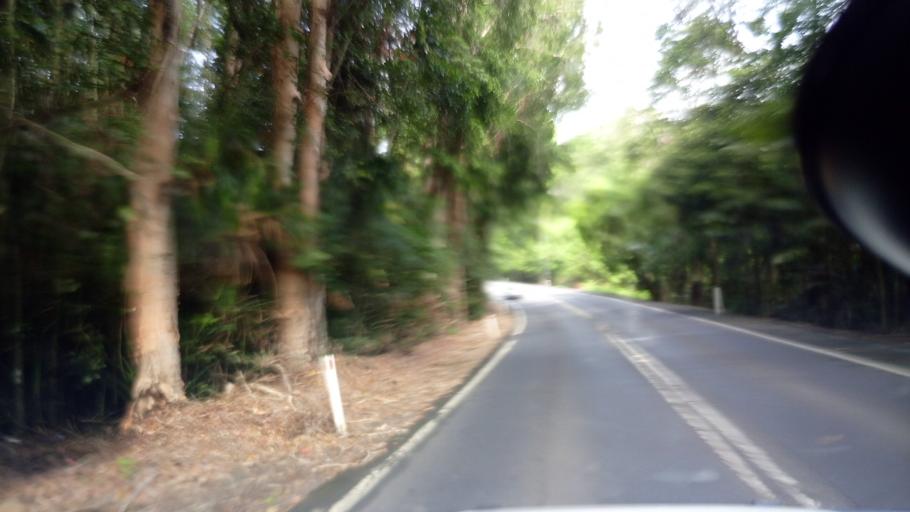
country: AU
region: Queensland
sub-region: Tablelands
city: Kuranda
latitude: -16.8142
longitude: 145.6395
